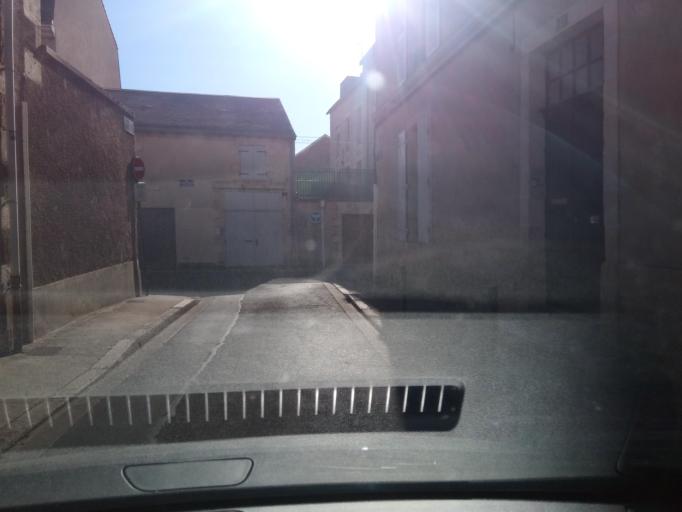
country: FR
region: Poitou-Charentes
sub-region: Departement de la Vienne
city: Poitiers
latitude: 46.5833
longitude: 0.3479
